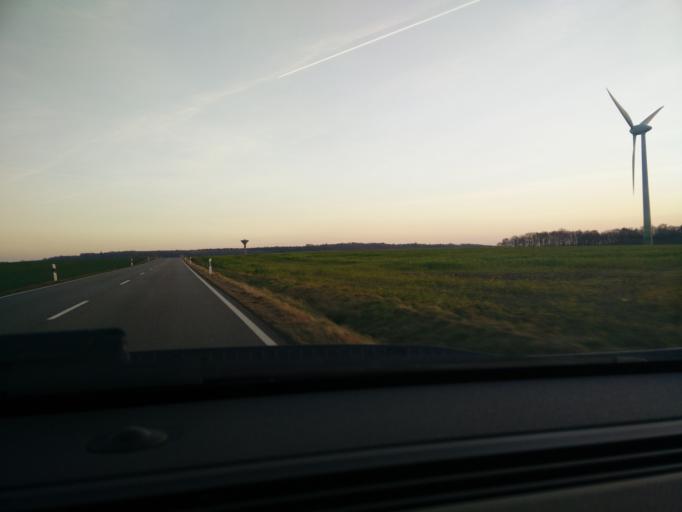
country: DE
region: Saxony
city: Geithain
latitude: 51.0944
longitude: 12.7028
